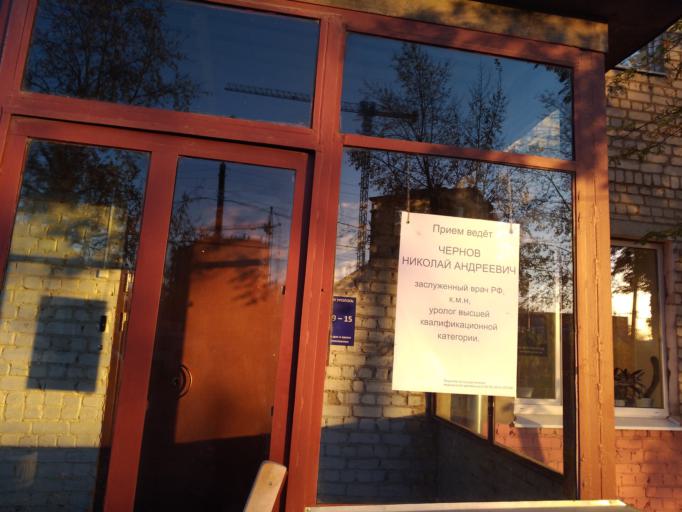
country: RU
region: Kaluga
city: Kaluga
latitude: 54.5209
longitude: 36.2825
